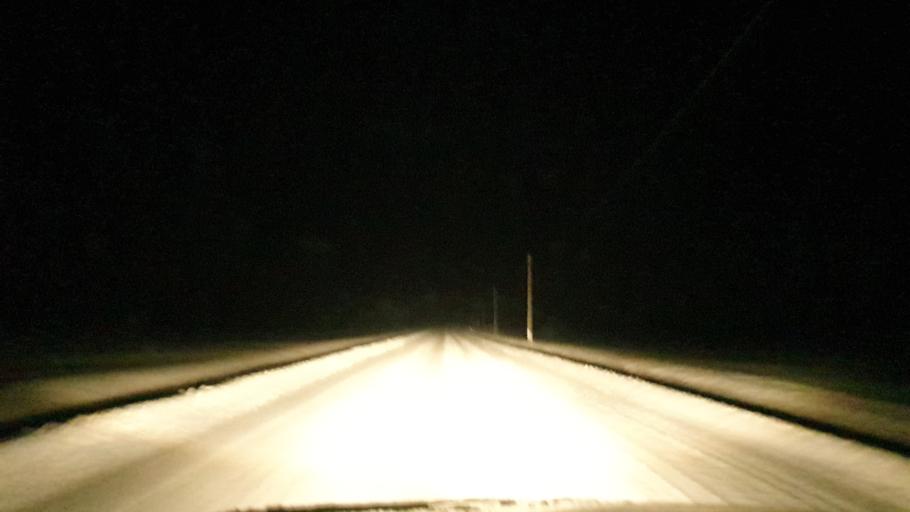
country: EE
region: Vorumaa
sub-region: Antsla vald
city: Vana-Antsla
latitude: 57.9604
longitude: 26.6730
